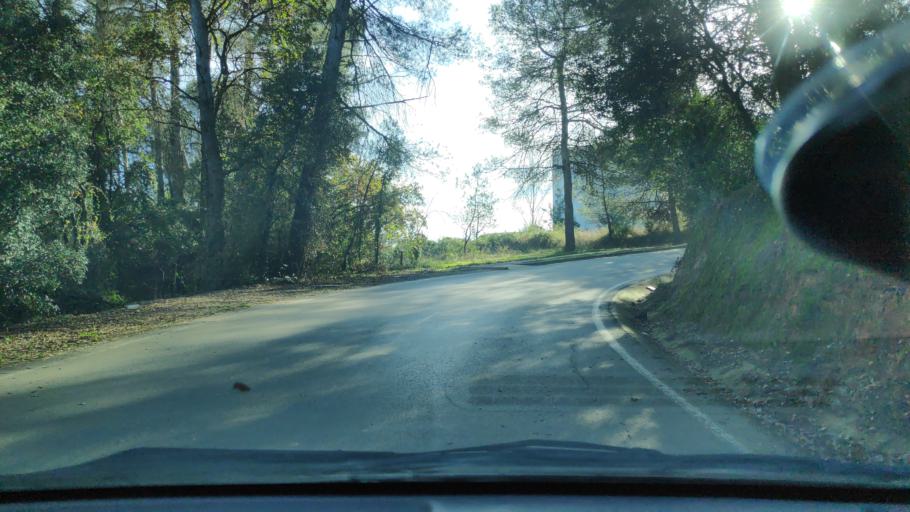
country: ES
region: Catalonia
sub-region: Provincia de Barcelona
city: Rubi
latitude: 41.4956
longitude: 2.0593
